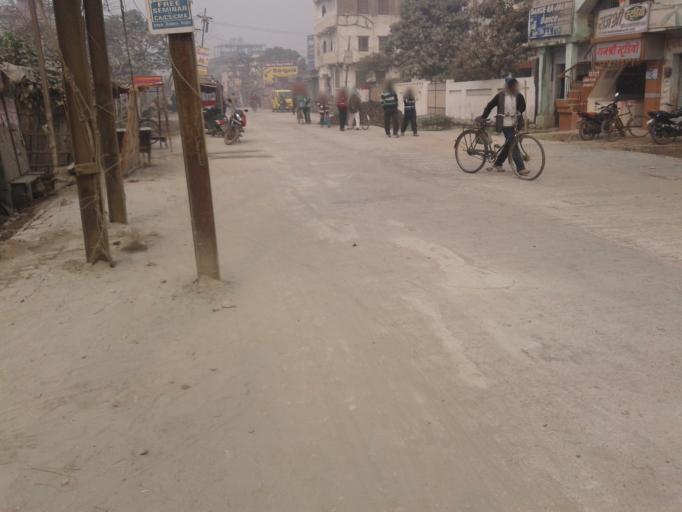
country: IN
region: Bihar
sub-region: Muzaffarpur
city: Muzaffarpur
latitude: 26.1332
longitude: 85.3633
